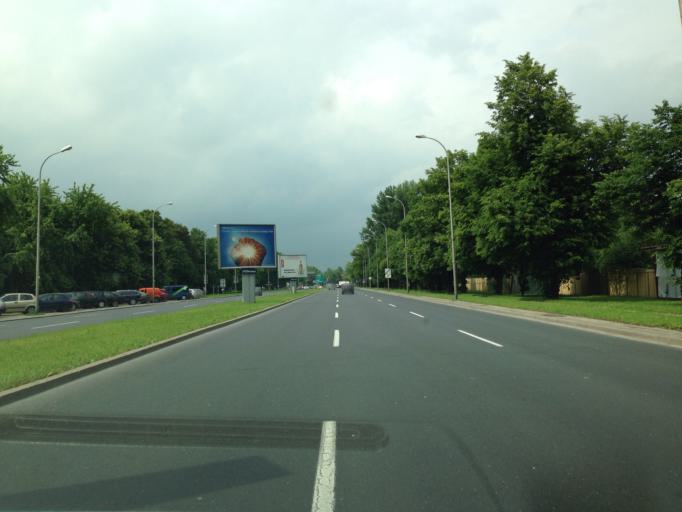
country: PL
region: Masovian Voivodeship
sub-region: Warszawa
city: Wlochy
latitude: 52.1762
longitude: 20.9791
